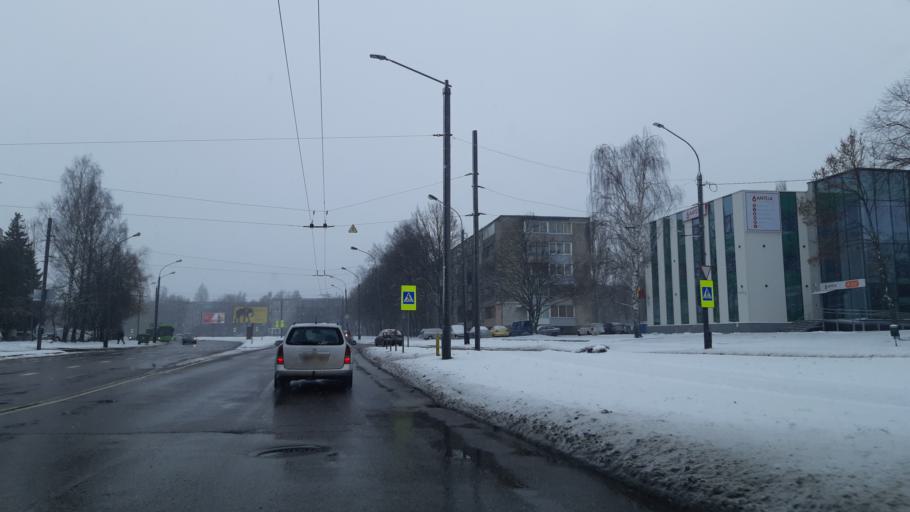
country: LT
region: Kauno apskritis
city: Dainava (Kaunas)
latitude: 54.9127
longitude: 23.9564
